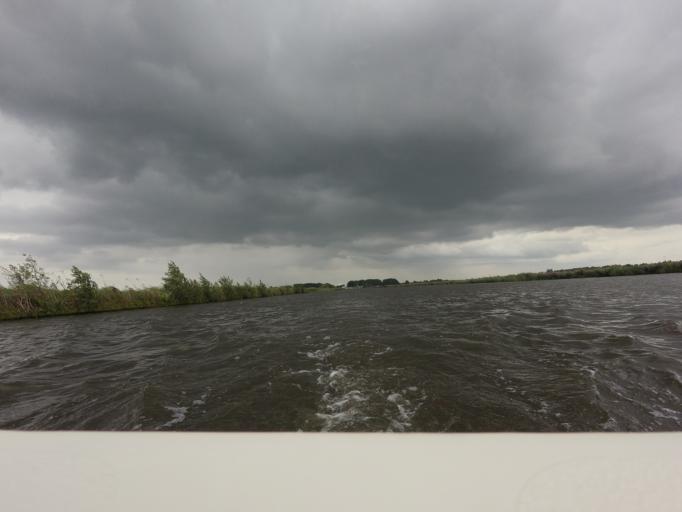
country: NL
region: Friesland
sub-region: Gemeente Smallingerland
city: Oudega
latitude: 53.1126
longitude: 5.9471
